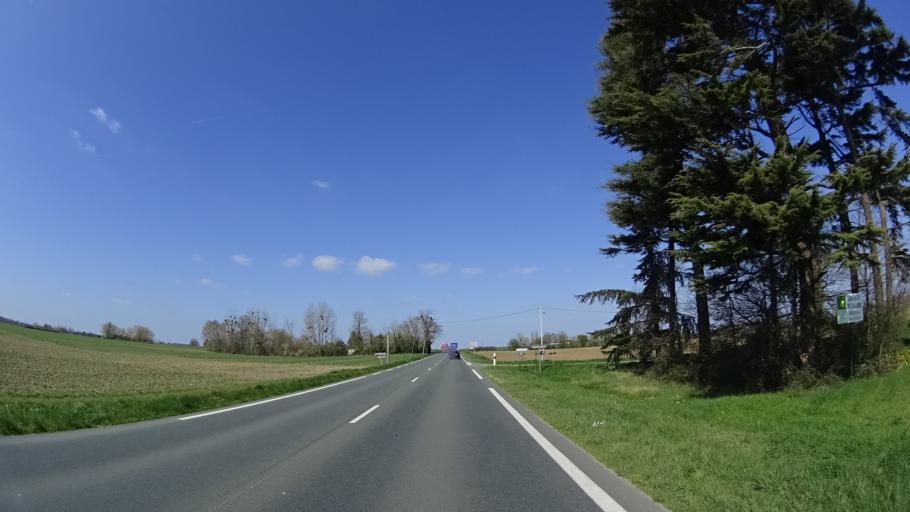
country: FR
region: Pays de la Loire
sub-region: Departement de Maine-et-Loire
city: Brissac-Quince
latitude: 47.3326
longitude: -0.4243
